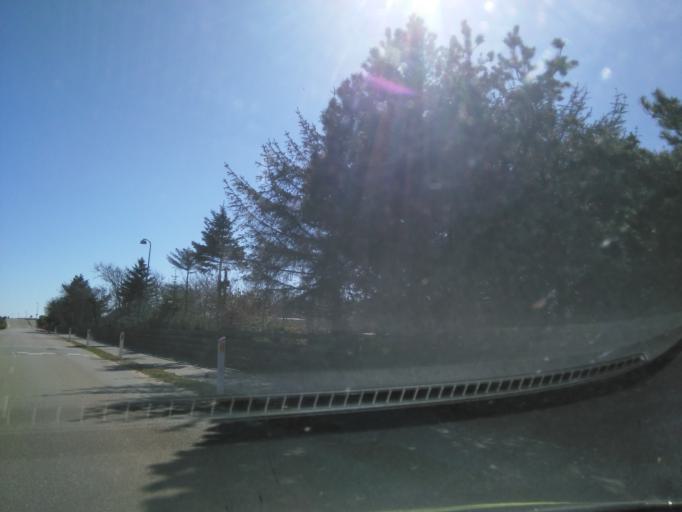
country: DK
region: South Denmark
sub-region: Varde Kommune
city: Oksbol
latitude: 55.5470
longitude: 8.1339
